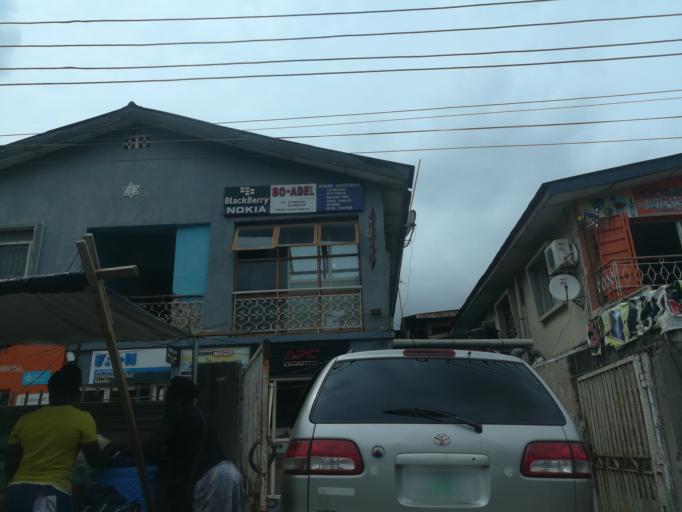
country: NG
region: Lagos
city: Ikeja
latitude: 6.5944
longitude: 3.3401
